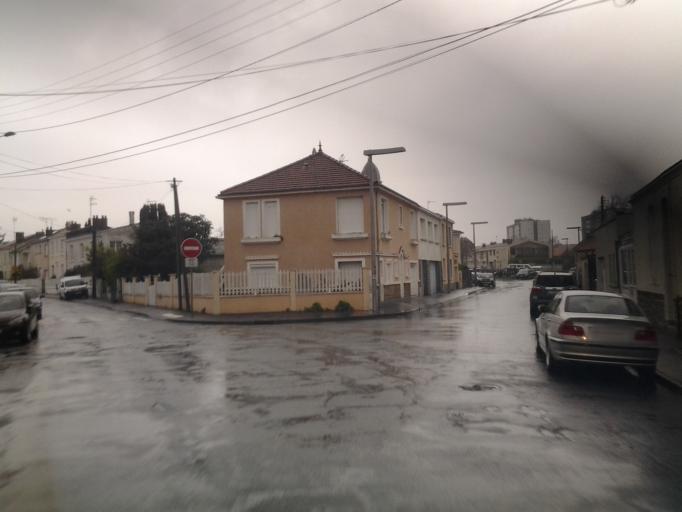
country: FR
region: Pays de la Loire
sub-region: Departement de la Vendee
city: La Roche-sur-Yon
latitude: 46.6757
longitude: -1.4328
